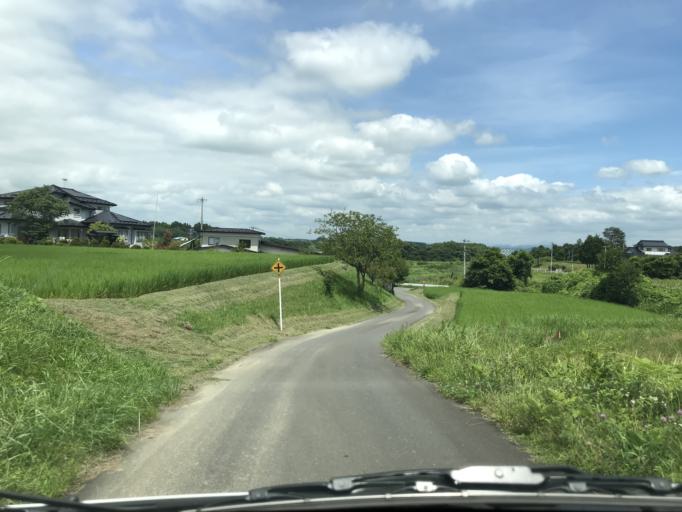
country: JP
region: Miyagi
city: Wakuya
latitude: 38.6779
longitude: 141.1149
